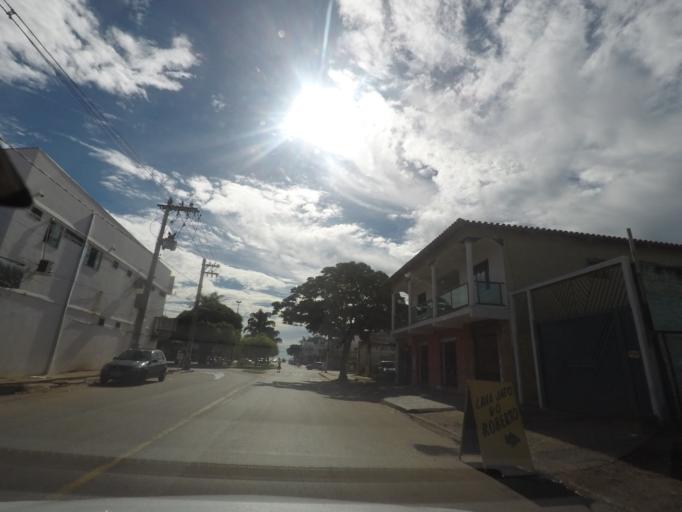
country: BR
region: Goias
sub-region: Aparecida De Goiania
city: Aparecida de Goiania
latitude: -16.8240
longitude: -49.2837
